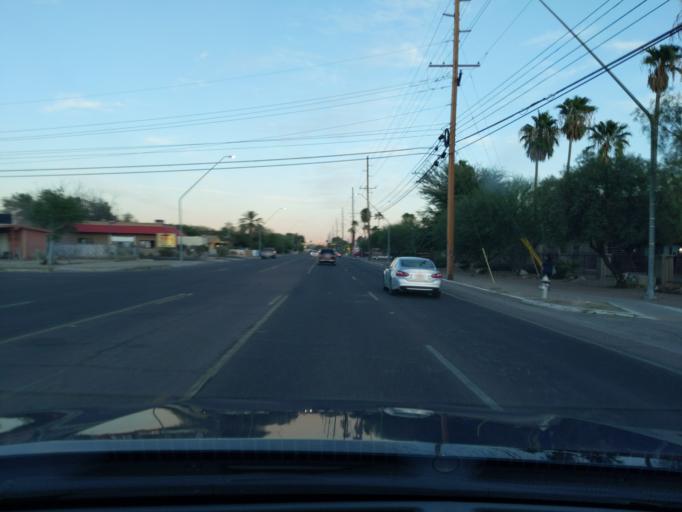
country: US
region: Arizona
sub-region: Pima County
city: South Tucson
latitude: 32.2290
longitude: -110.9953
